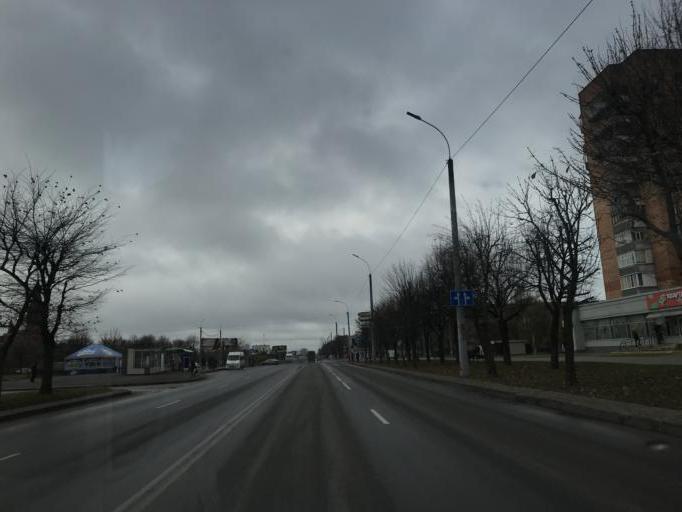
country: BY
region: Mogilev
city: Mahilyow
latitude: 53.8714
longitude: 30.3254
